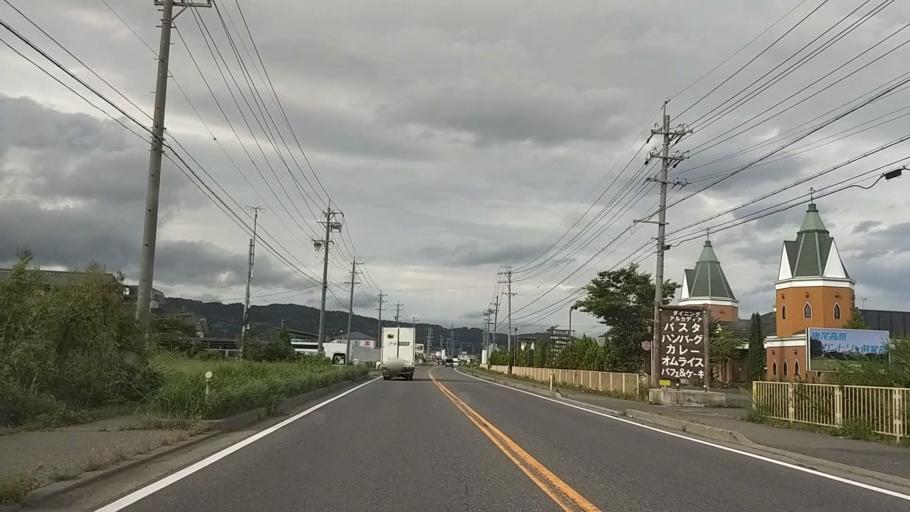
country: JP
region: Nagano
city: Suzaka
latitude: 36.6919
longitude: 138.2685
